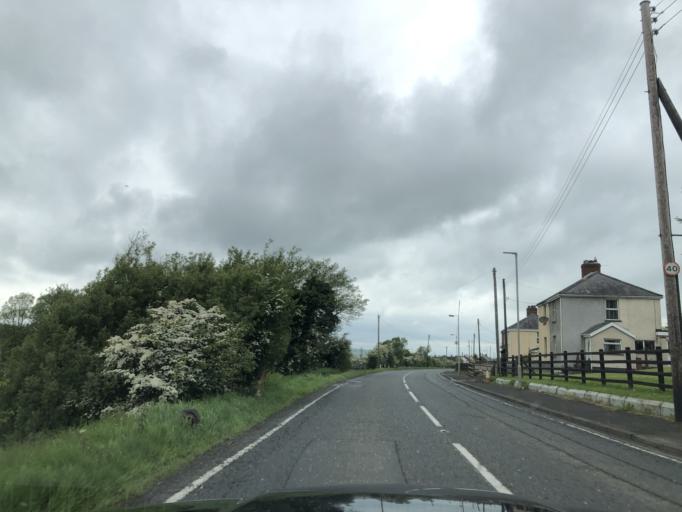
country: GB
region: Northern Ireland
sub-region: Lisburn District
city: Lisburn
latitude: 54.5511
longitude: -6.0849
